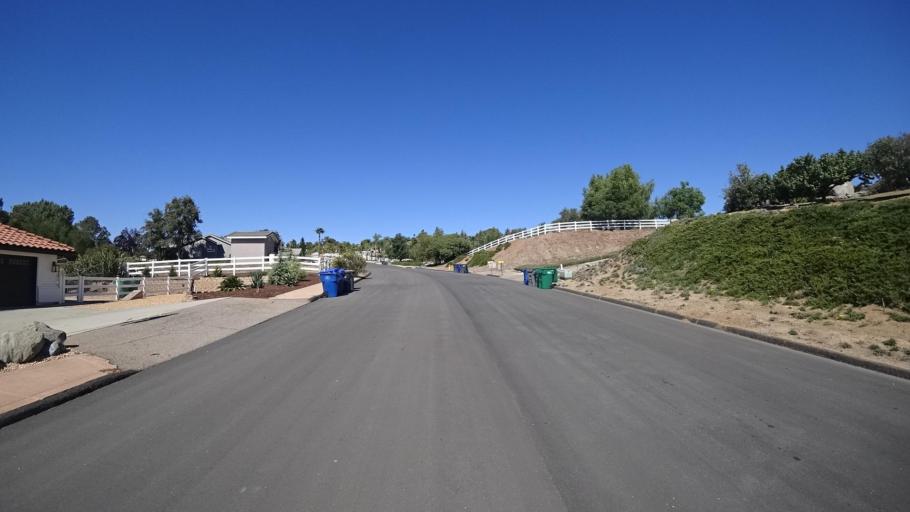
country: US
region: California
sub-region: San Diego County
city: Alpine
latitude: 32.8410
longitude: -116.7617
